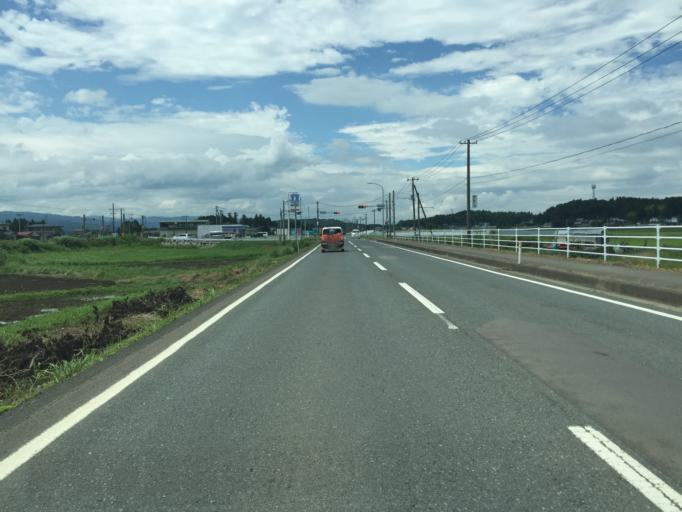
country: JP
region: Fukushima
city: Namie
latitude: 37.7117
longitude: 140.9633
